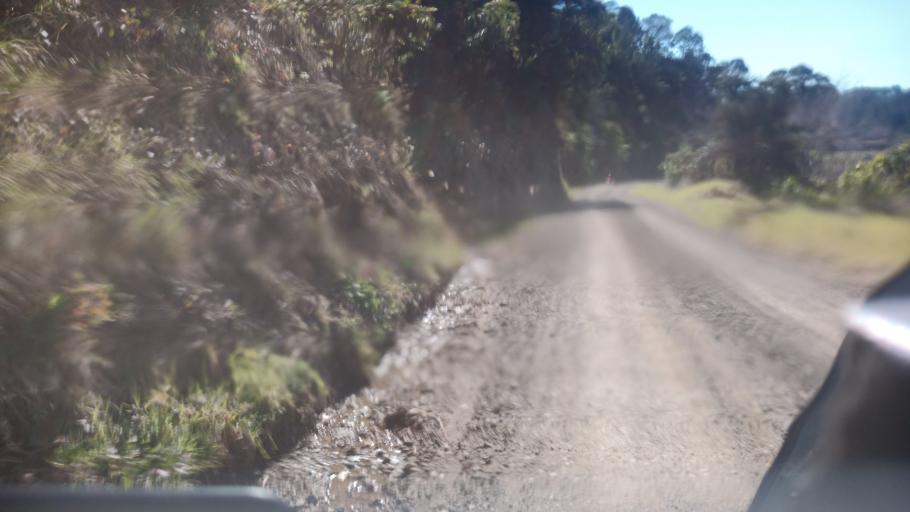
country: NZ
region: Bay of Plenty
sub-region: Opotiki District
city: Opotiki
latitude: -38.0297
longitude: 177.4409
